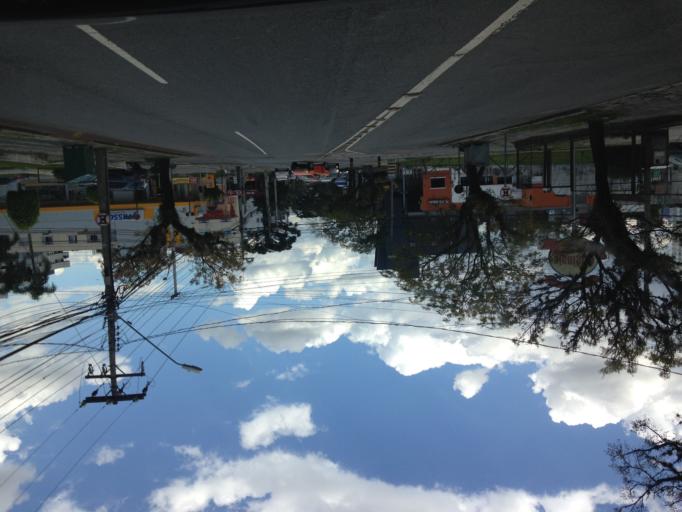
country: BR
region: Parana
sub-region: Curitiba
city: Curitiba
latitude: -25.4097
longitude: -49.2527
